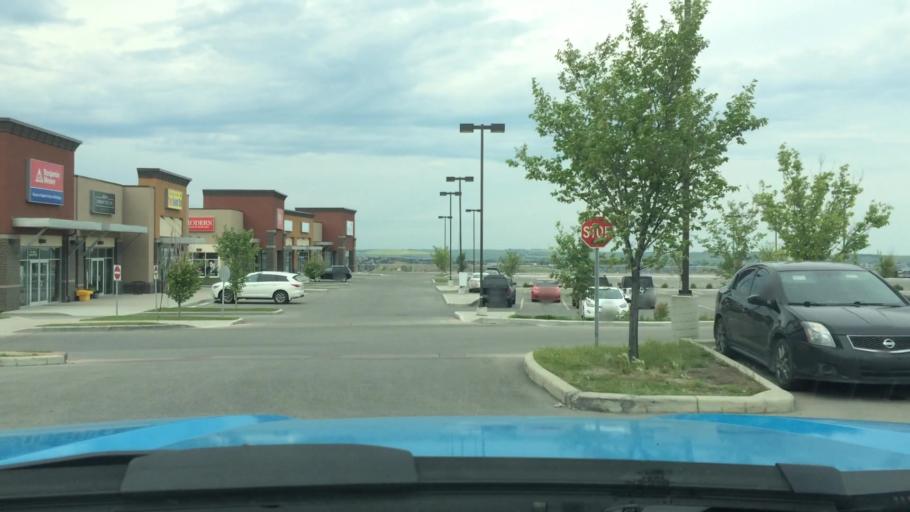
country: CA
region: Alberta
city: Calgary
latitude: 51.1613
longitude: -114.1617
